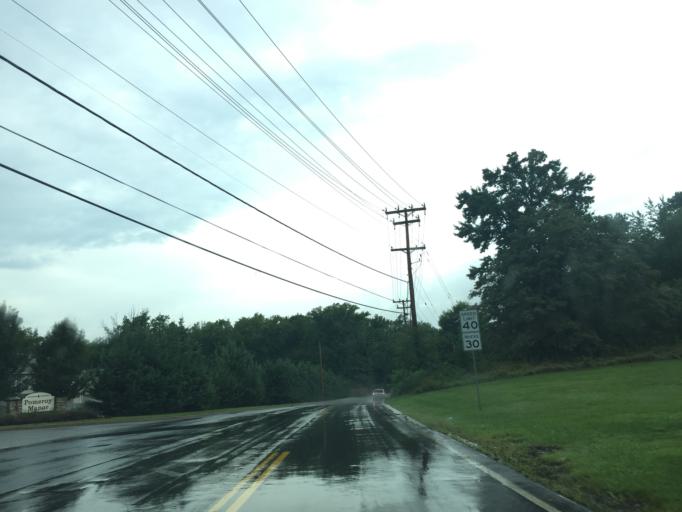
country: US
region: Maryland
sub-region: Harford County
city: Riverside
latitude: 39.4629
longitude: -76.2801
